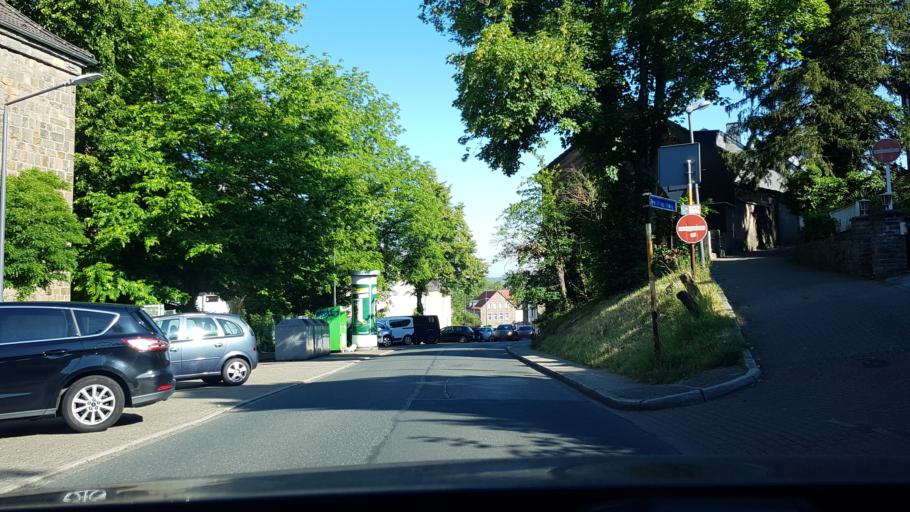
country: DE
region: North Rhine-Westphalia
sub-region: Regierungsbezirk Dusseldorf
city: Velbert
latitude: 51.3958
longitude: 7.0872
